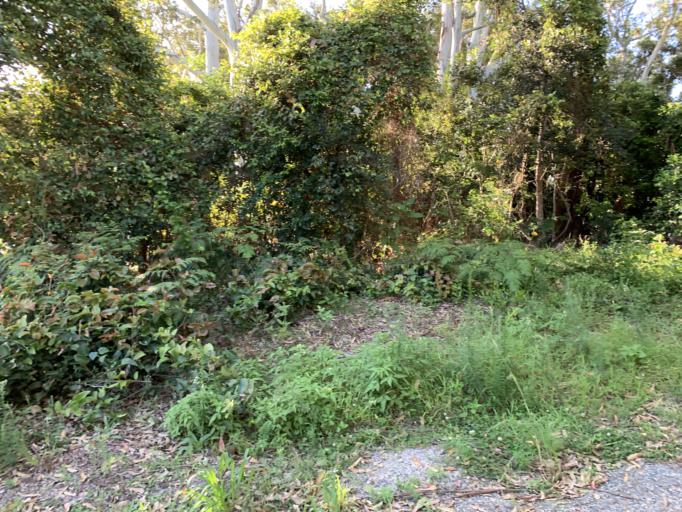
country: AU
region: New South Wales
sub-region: Port Macquarie-Hastings
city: North Haven
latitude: -31.6496
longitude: 152.8240
